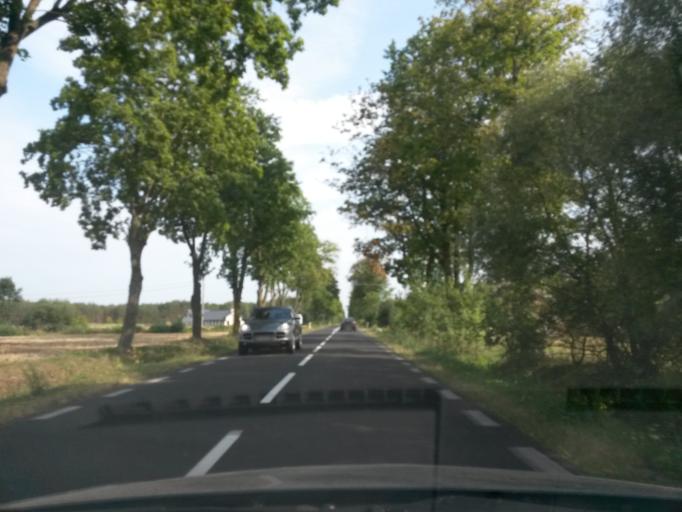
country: PL
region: Masovian Voivodeship
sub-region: Powiat sierpecki
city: Sierpc
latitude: 52.9098
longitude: 19.6330
